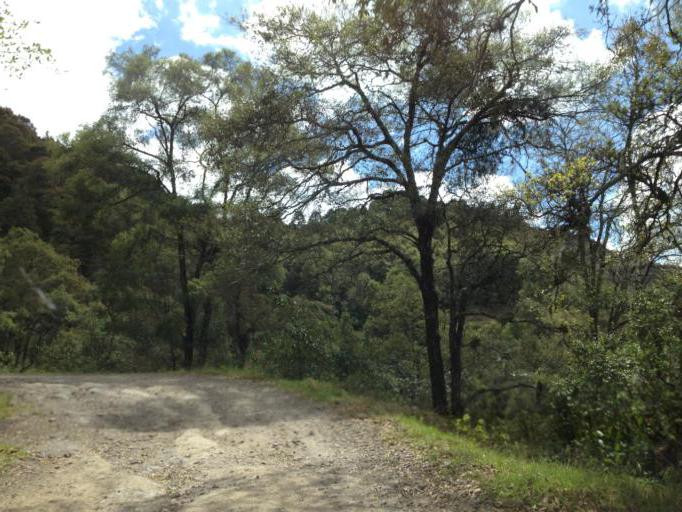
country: MX
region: Hidalgo
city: Mineral del Monte
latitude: 20.2091
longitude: -98.6783
